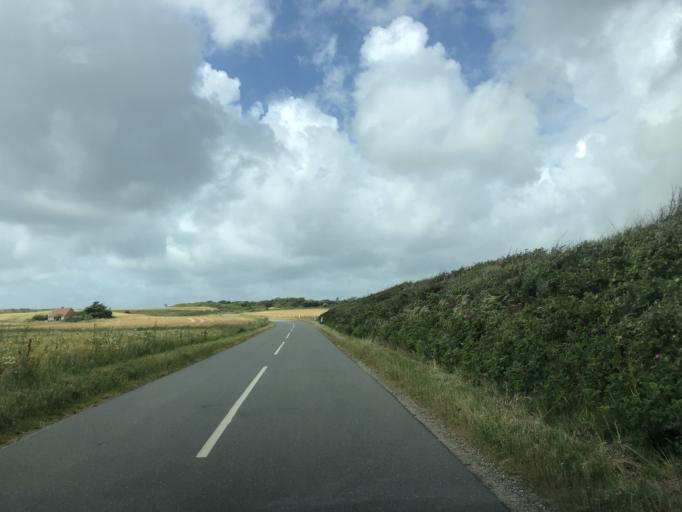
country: DK
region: Central Jutland
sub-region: Lemvig Kommune
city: Harboore
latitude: 56.4899
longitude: 8.1371
